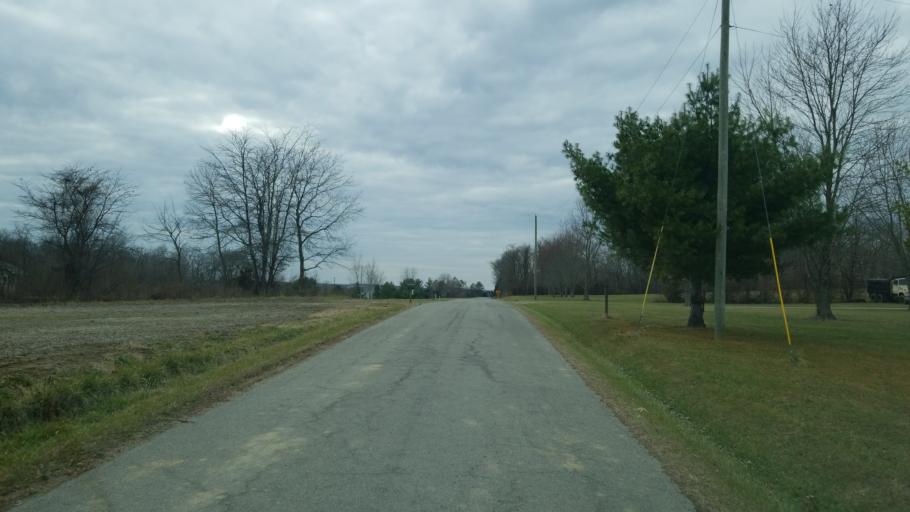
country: US
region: Ohio
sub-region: Highland County
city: Greenfield
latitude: 39.2981
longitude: -83.3609
